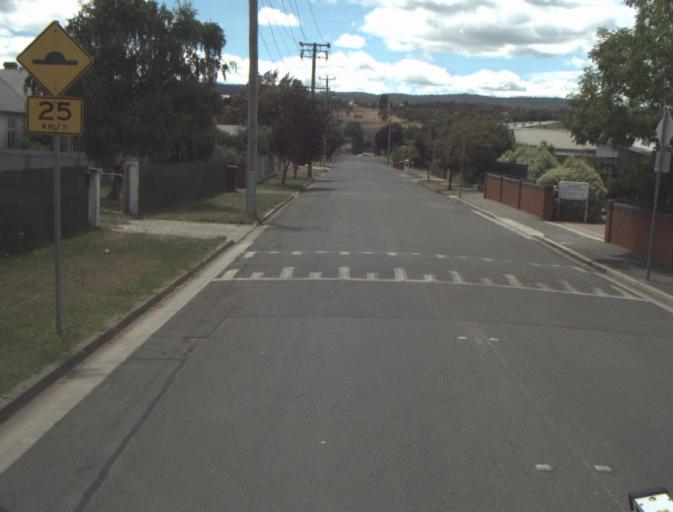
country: AU
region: Tasmania
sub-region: Launceston
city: Newstead
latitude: -41.4318
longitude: 147.1579
